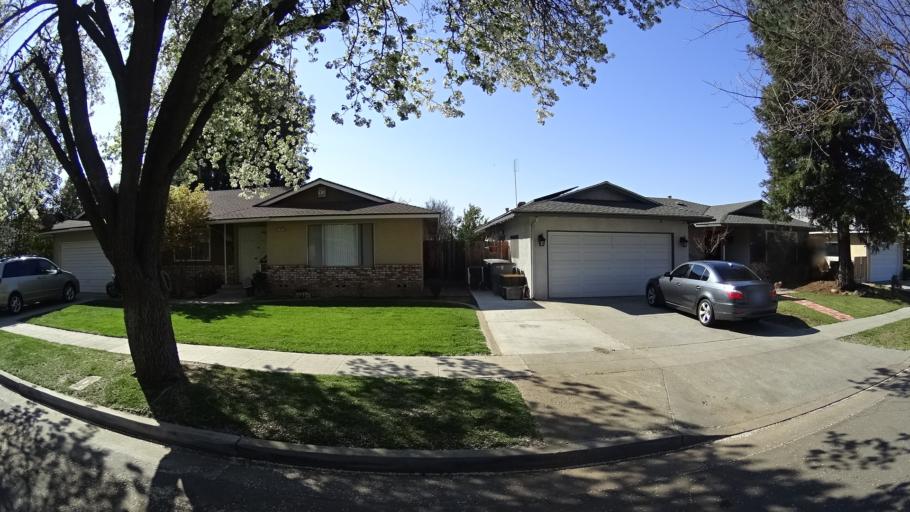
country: US
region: California
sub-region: Fresno County
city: Clovis
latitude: 36.8271
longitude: -119.7306
